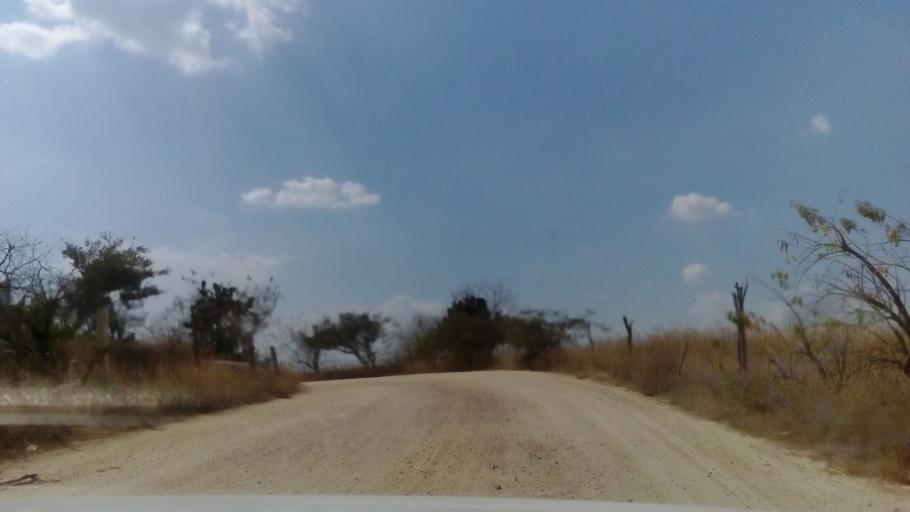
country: MX
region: Guanajuato
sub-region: Silao de la Victoria
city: Loma de Yerbabuena
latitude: 21.0884
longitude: -101.4418
